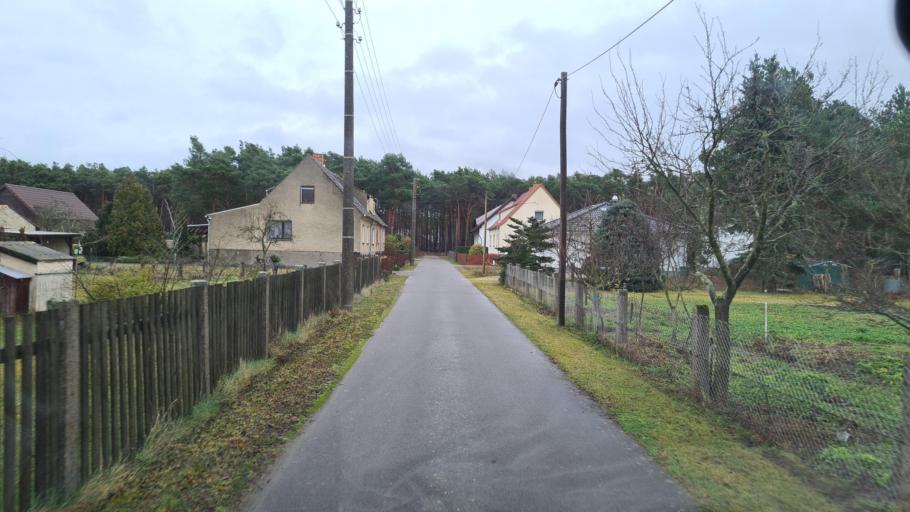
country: DE
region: Brandenburg
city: Schlepzig
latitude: 51.9847
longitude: 13.9751
